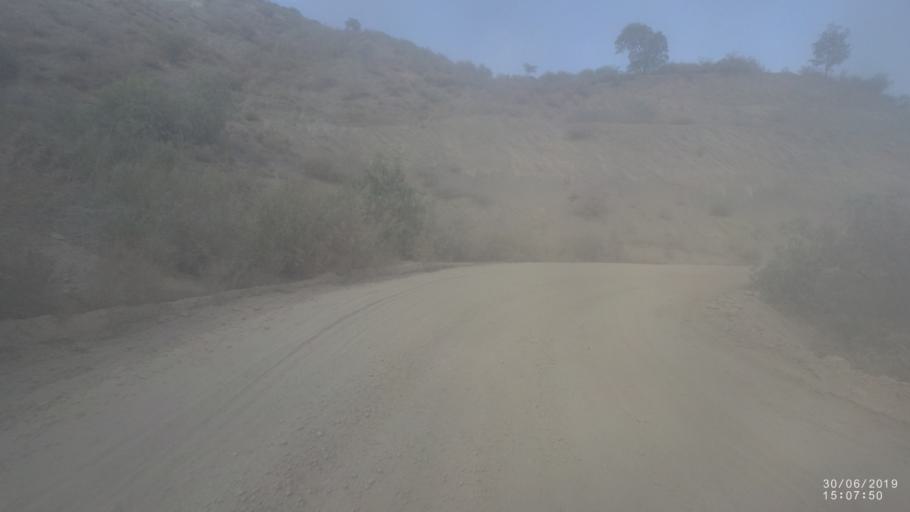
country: BO
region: Cochabamba
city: Irpa Irpa
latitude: -17.7305
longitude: -66.3045
